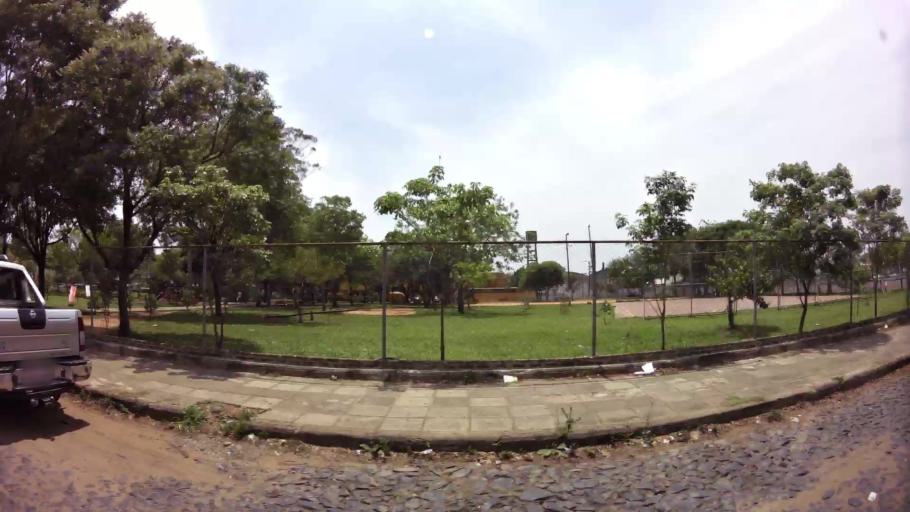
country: PY
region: Central
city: Lambare
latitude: -25.3152
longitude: -57.5707
